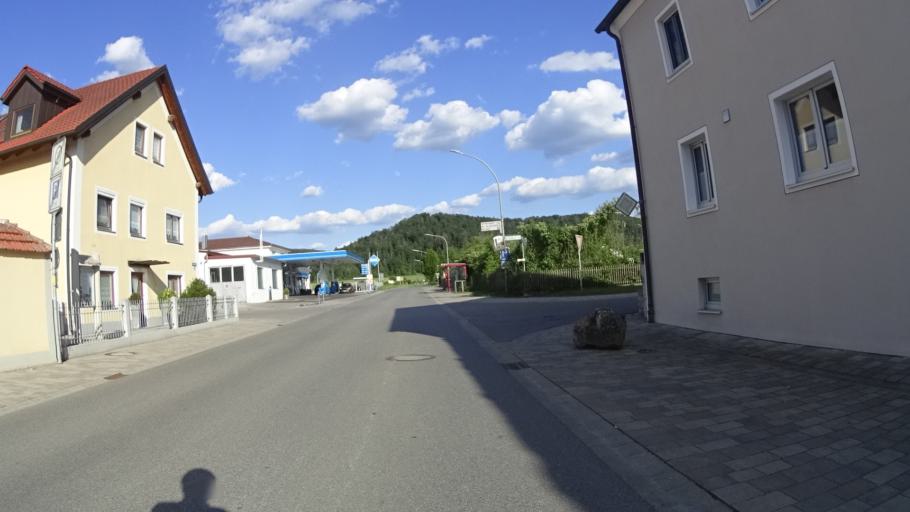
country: DE
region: Bavaria
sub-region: Upper Palatinate
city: Dietfurt
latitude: 49.0336
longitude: 11.5923
